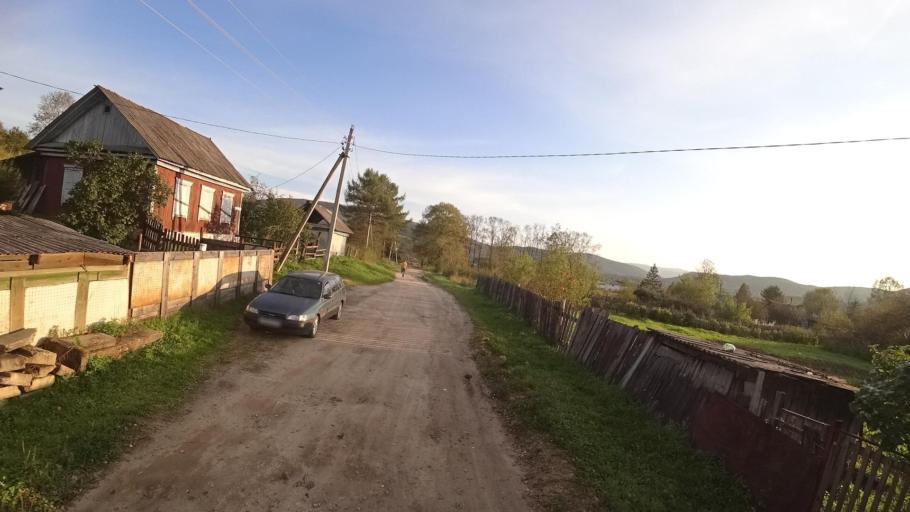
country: RU
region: Jewish Autonomous Oblast
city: Kul'dur
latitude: 49.2097
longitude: 131.6414
